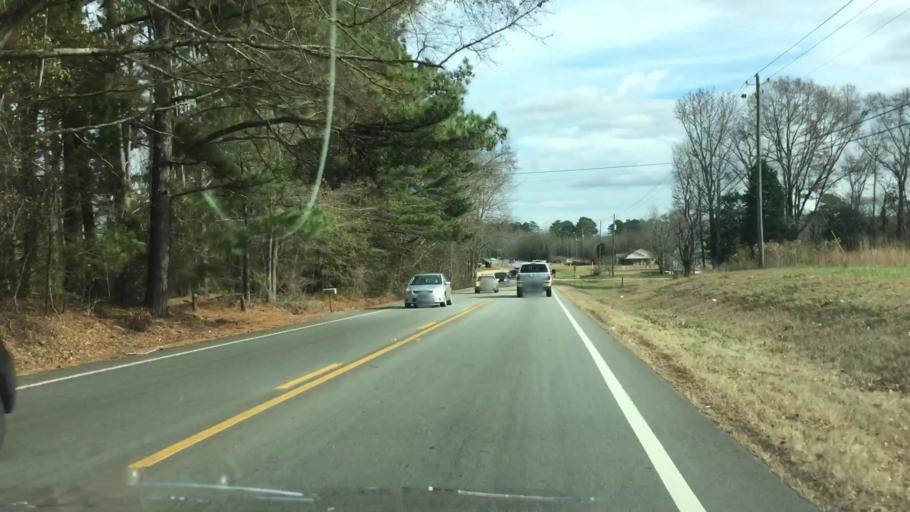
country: US
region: Georgia
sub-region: Henry County
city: McDonough
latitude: 33.4275
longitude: -84.0835
